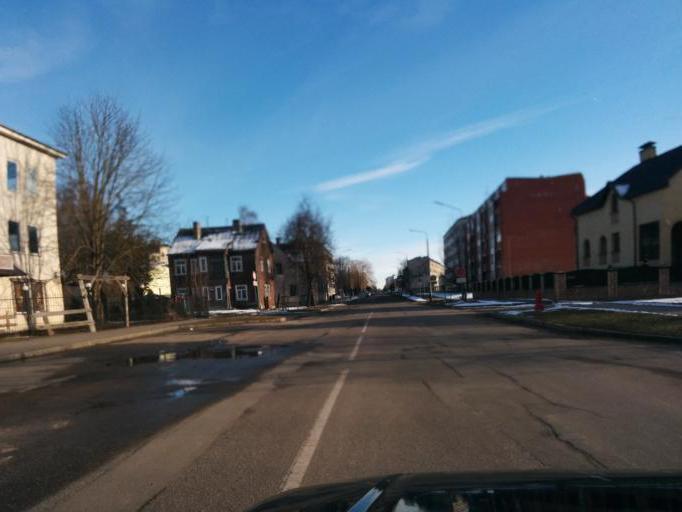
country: LV
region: Jelgava
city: Jelgava
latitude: 56.6567
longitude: 23.7186
